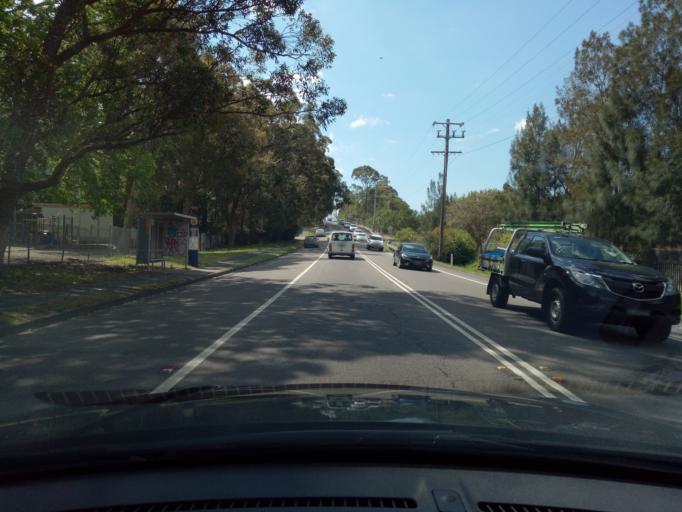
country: AU
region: New South Wales
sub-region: Gosford Shire
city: Point Clare
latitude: -33.4438
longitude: 151.3289
